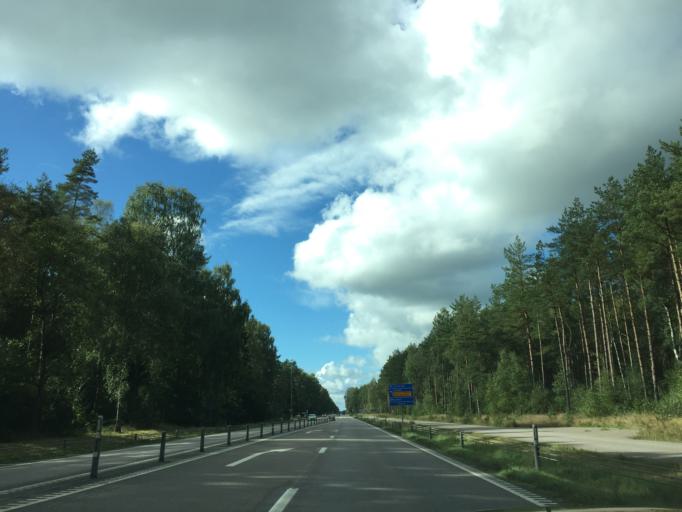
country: SE
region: Skane
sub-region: Sjobo Kommun
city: Sjoebo
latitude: 55.6372
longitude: 13.6584
